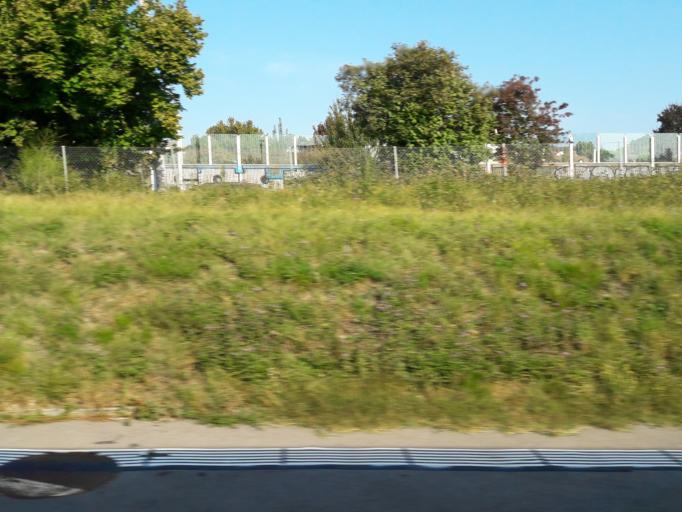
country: CH
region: Vaud
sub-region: Morges District
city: Preverenges
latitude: 46.5287
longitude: 6.5397
